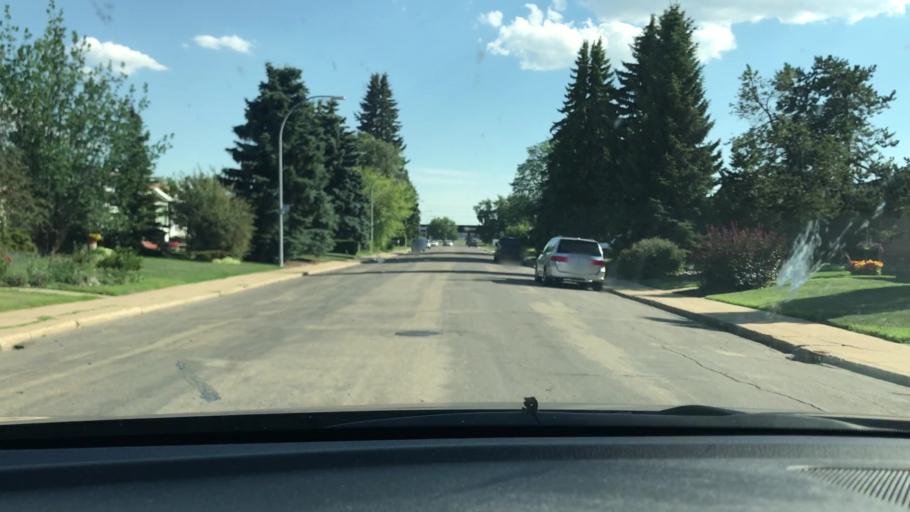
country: CA
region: Alberta
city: Edmonton
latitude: 53.5210
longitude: -113.4228
